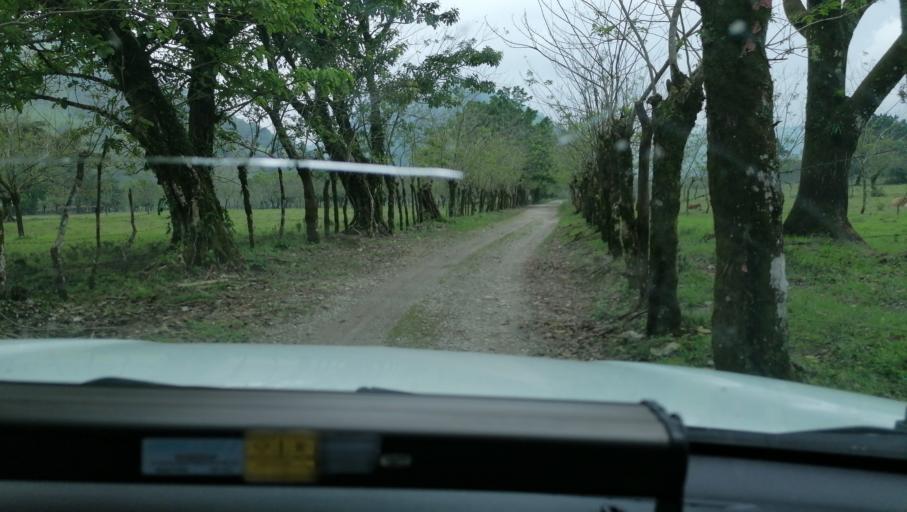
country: MX
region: Chiapas
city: Ixtacomitan
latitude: 17.3651
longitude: -93.1756
